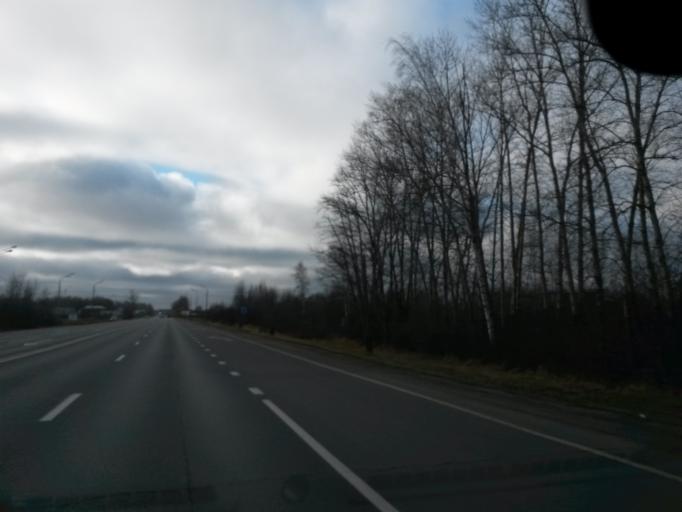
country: RU
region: Jaroslavl
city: Semibratovo
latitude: 57.3086
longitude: 39.5470
